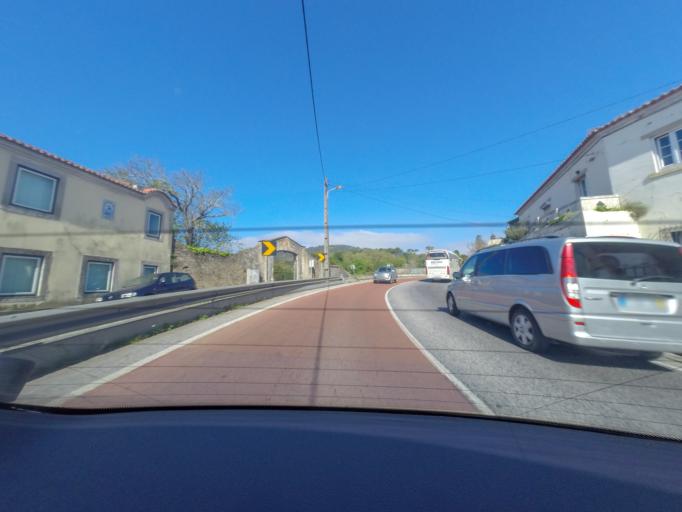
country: PT
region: Lisbon
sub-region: Sintra
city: Sintra
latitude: 38.7837
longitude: -9.3701
